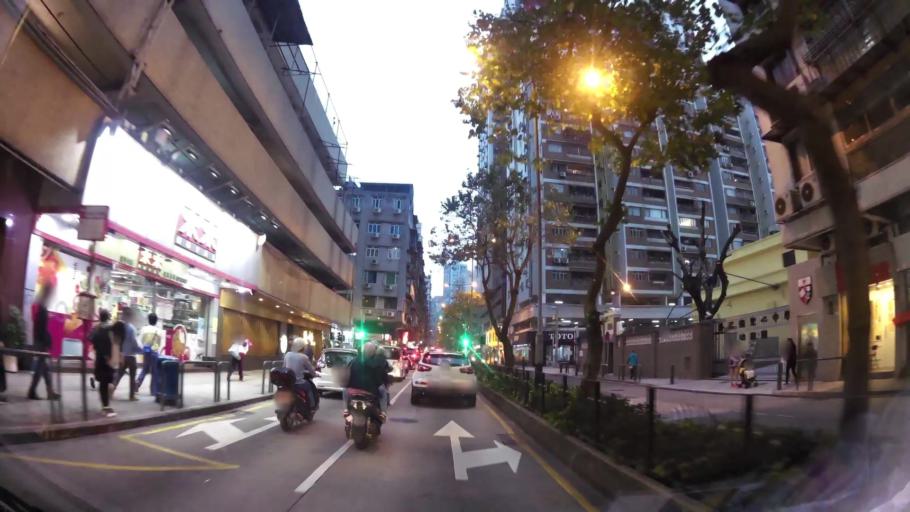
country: MO
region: Macau
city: Macau
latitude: 22.2036
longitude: 113.5483
